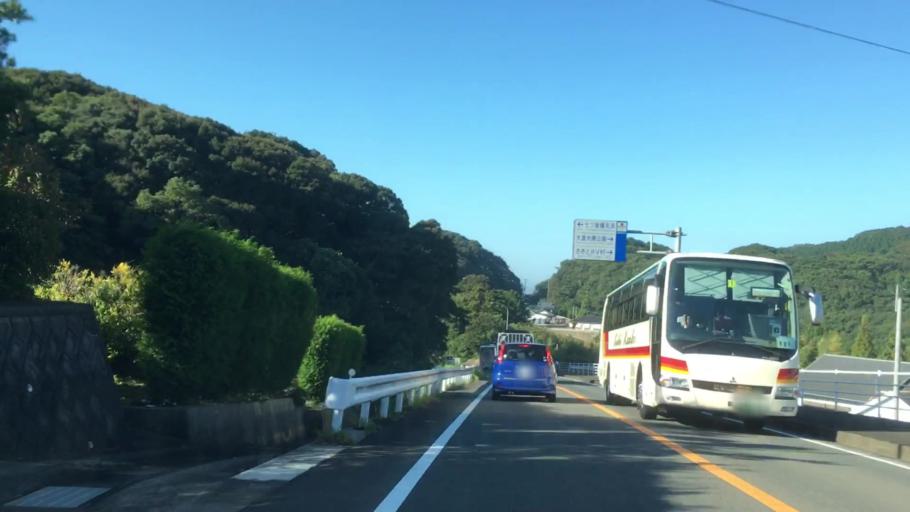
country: JP
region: Nagasaki
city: Sasebo
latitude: 33.0355
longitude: 129.6650
